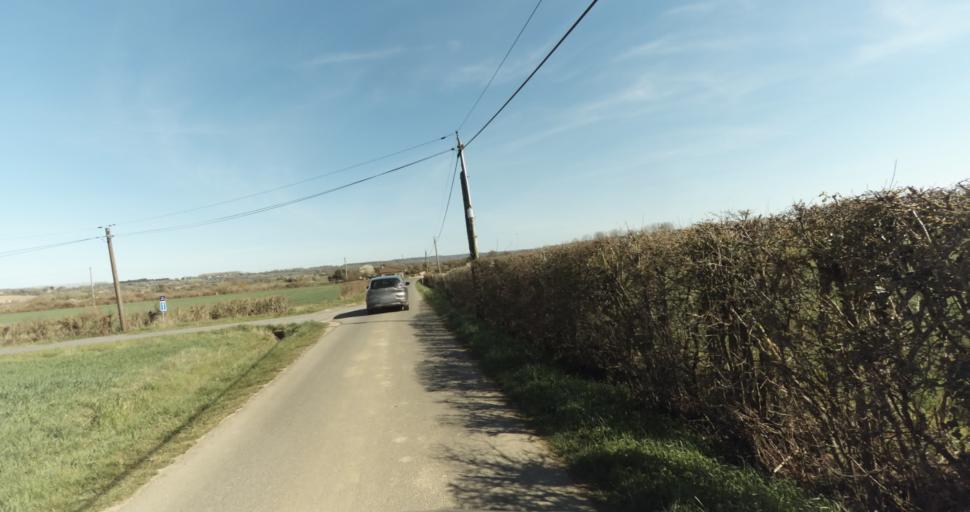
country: FR
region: Lower Normandy
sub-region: Departement du Calvados
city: Saint-Pierre-sur-Dives
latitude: 49.0487
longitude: -0.0159
